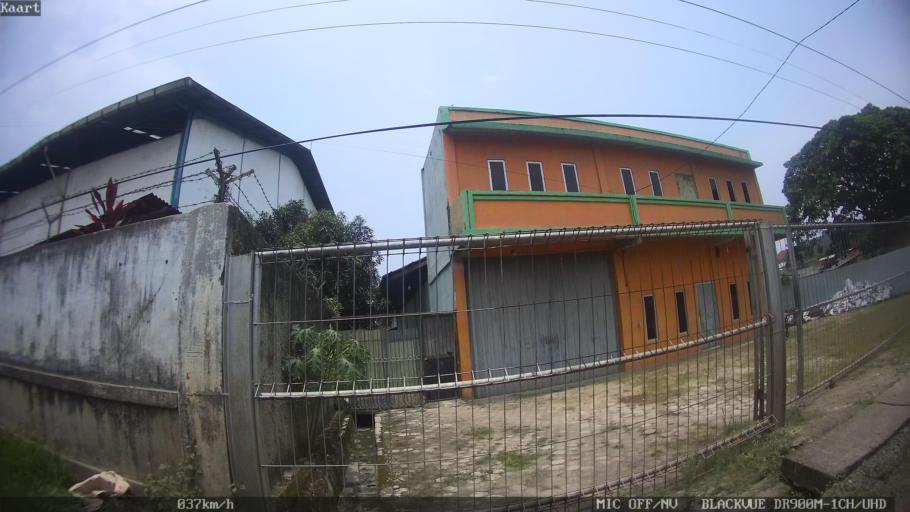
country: ID
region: Lampung
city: Bandarlampung
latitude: -5.4061
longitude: 105.2905
